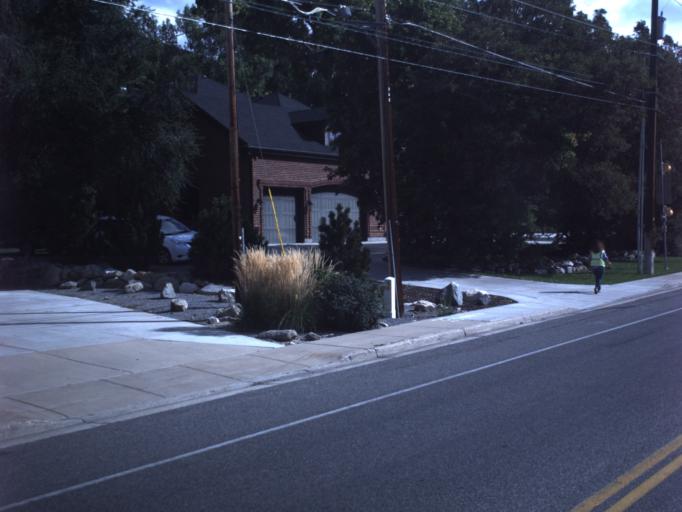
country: US
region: Utah
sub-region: Davis County
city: Farmington
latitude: 40.9768
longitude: -111.8833
